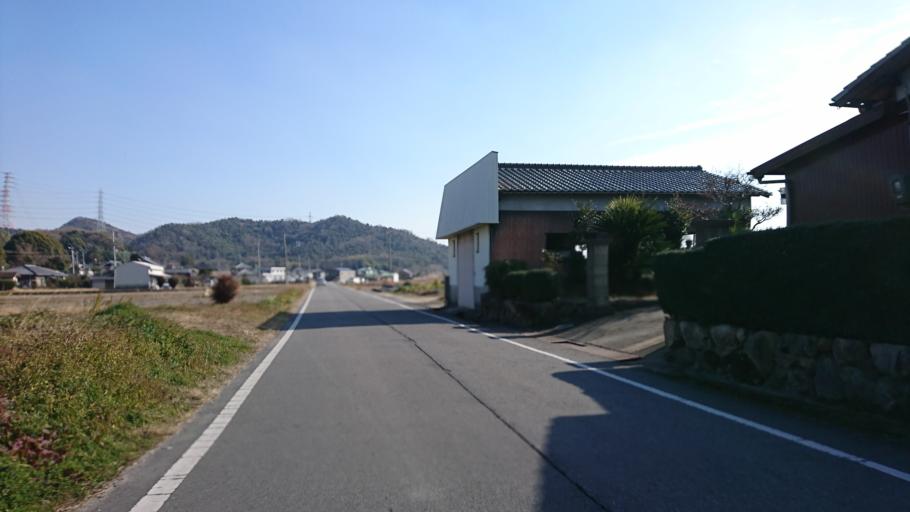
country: JP
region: Hyogo
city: Kakogawacho-honmachi
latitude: 34.8210
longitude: 134.8490
